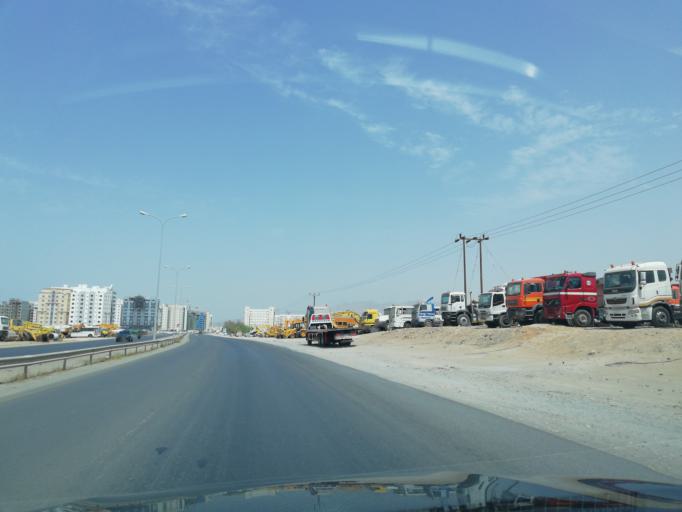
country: OM
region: Muhafazat Masqat
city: Bawshar
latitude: 23.5826
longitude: 58.3615
